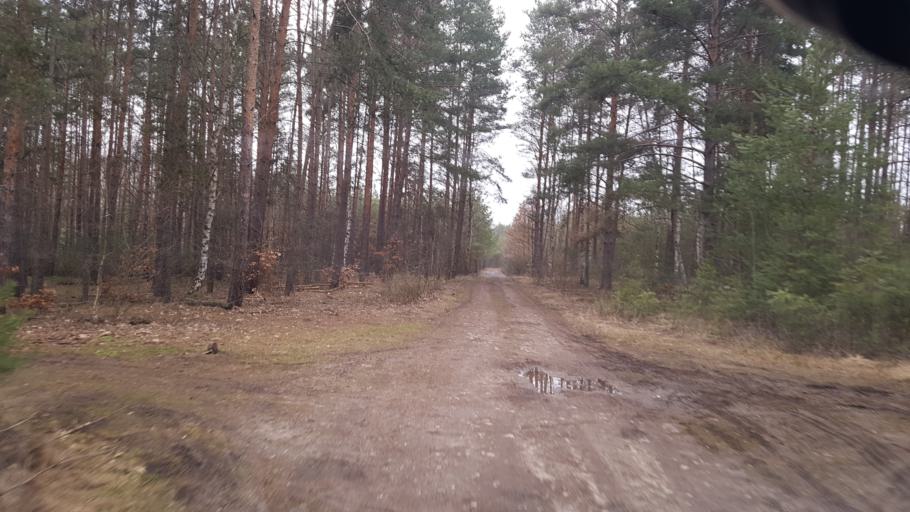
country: DE
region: Brandenburg
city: Trobitz
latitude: 51.6114
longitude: 13.4576
